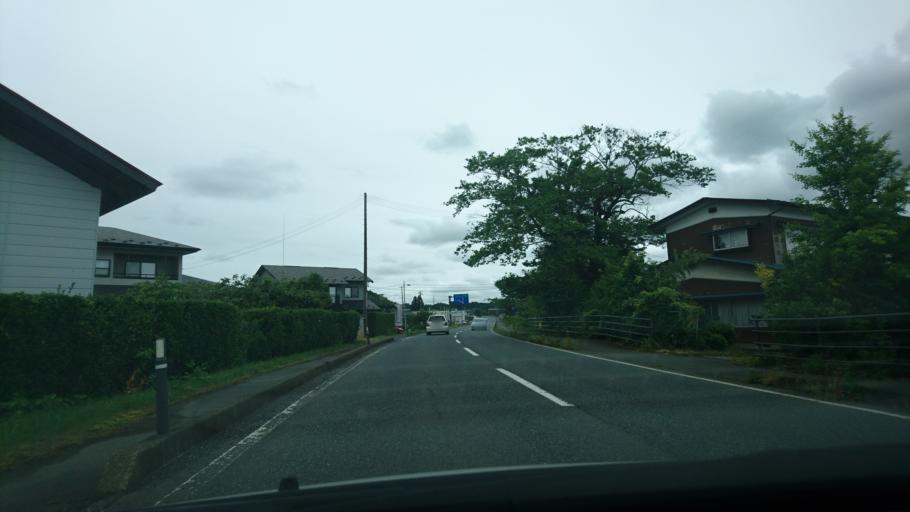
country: JP
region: Iwate
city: Ichinoseki
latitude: 39.0092
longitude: 141.1087
